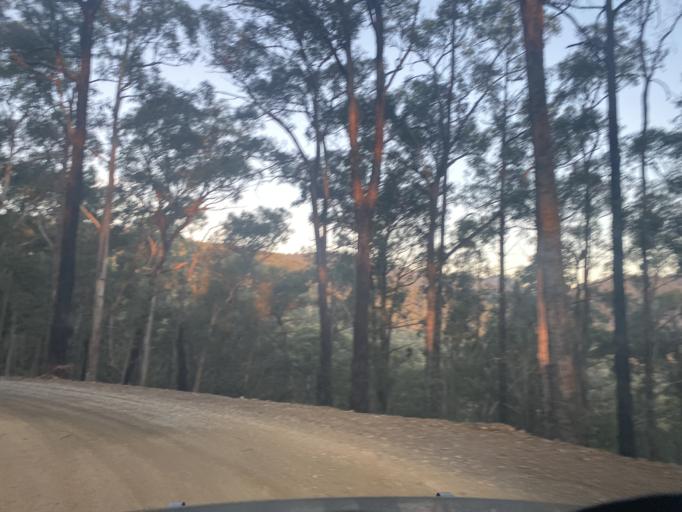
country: AU
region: Victoria
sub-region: Yarra Ranges
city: Healesville
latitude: -37.4269
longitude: 145.5133
